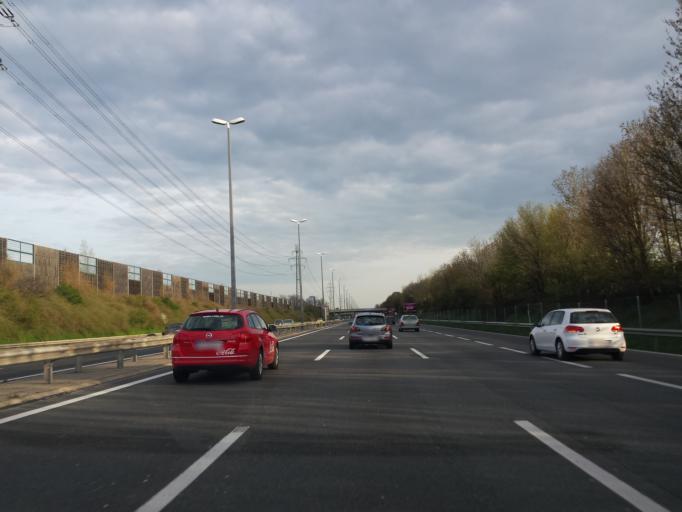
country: AT
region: Lower Austria
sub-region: Politischer Bezirk Korneuburg
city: Langenzersdorf
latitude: 48.2780
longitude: 16.3679
